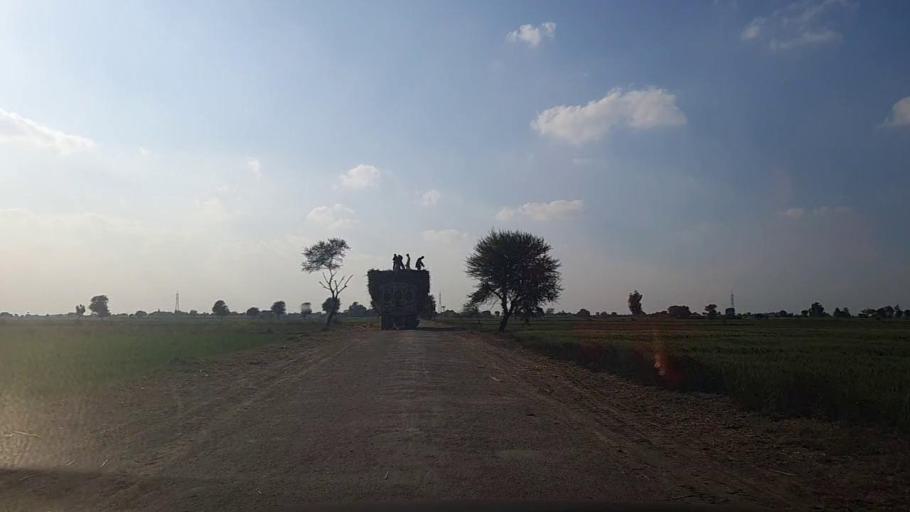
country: PK
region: Sindh
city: Jhol
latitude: 25.8381
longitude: 69.0623
